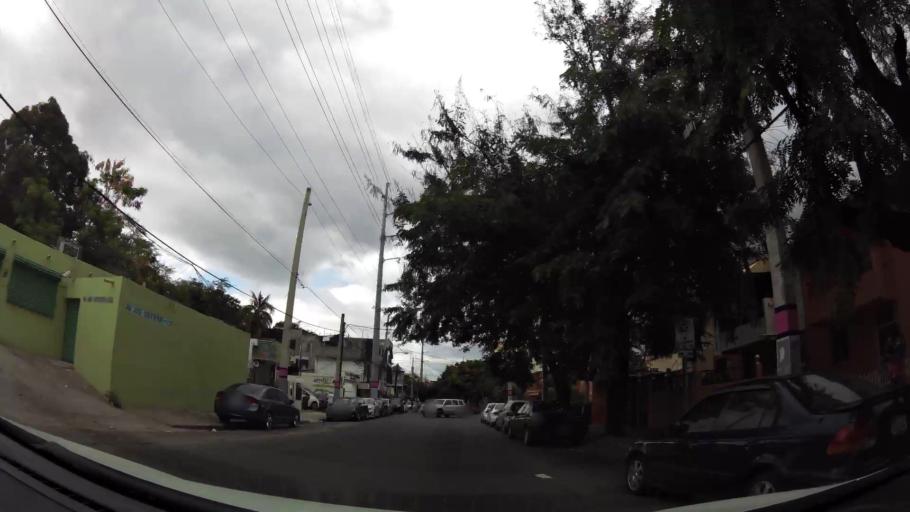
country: DO
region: Nacional
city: Bella Vista
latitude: 18.4528
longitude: -69.9329
